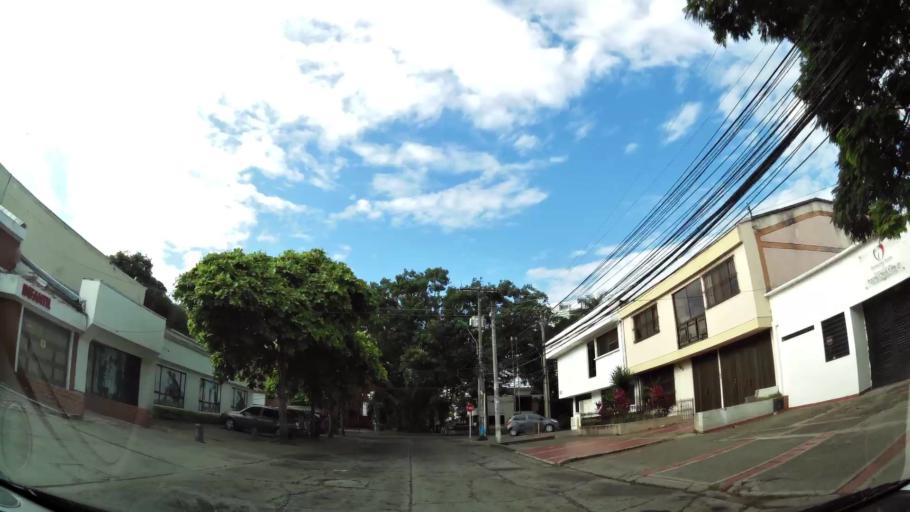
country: CO
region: Valle del Cauca
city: Cali
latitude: 3.4774
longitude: -76.5253
